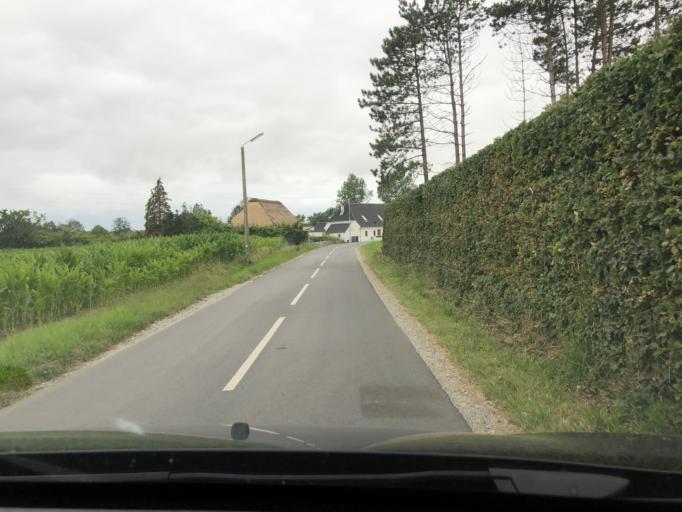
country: DK
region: South Denmark
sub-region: AEro Kommune
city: Marstal
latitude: 54.8550
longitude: 10.4838
